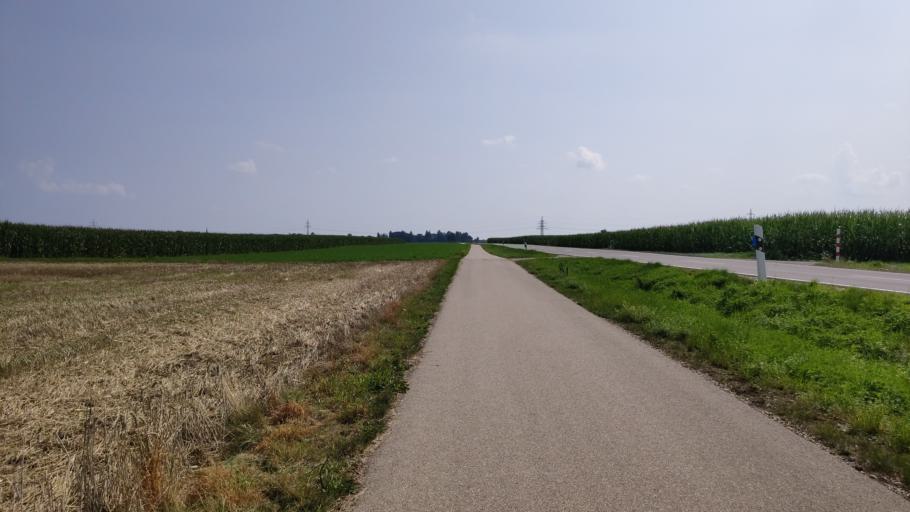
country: DE
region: Bavaria
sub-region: Swabia
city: Kleinaitingen
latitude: 48.2183
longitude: 10.8181
